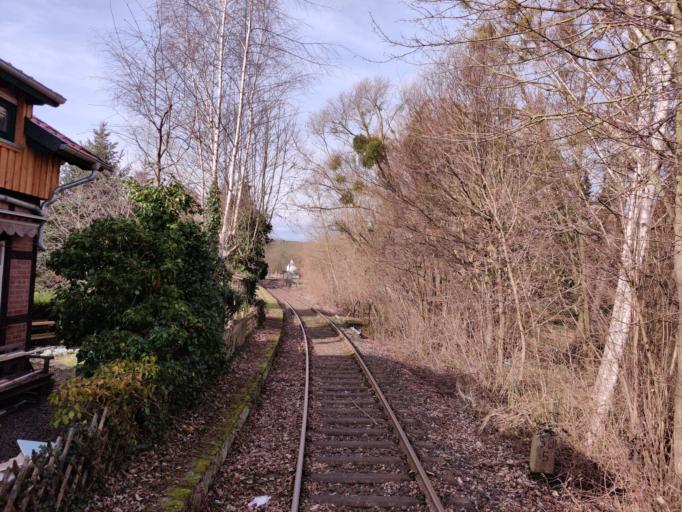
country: DE
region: Lower Saxony
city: Bockenem
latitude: 51.9838
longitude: 10.1173
